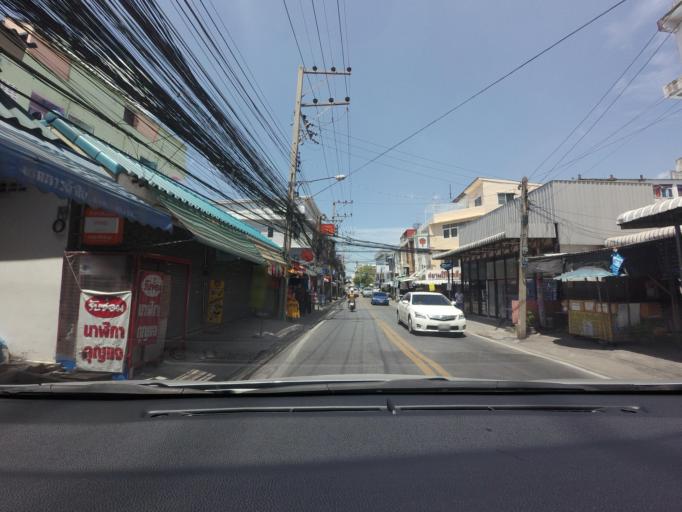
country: TH
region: Bangkok
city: Watthana
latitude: 13.7361
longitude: 100.6085
